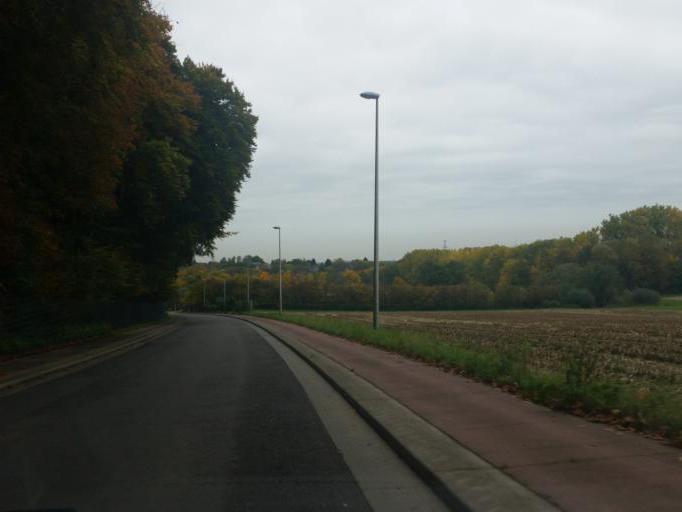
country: BE
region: Flanders
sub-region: Provincie Vlaams-Brabant
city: Beersel
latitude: 50.7473
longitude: 4.2898
